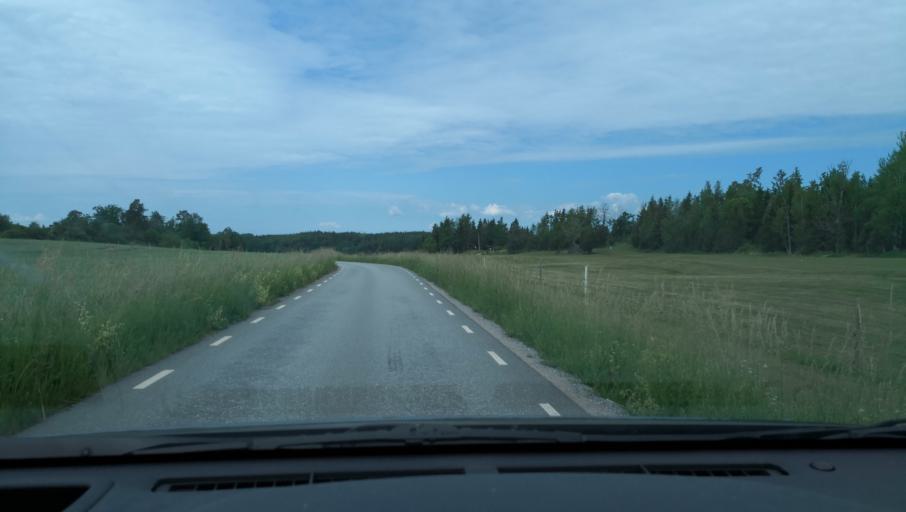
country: SE
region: Uppsala
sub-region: Habo Kommun
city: Balsta
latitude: 59.6992
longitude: 17.4787
